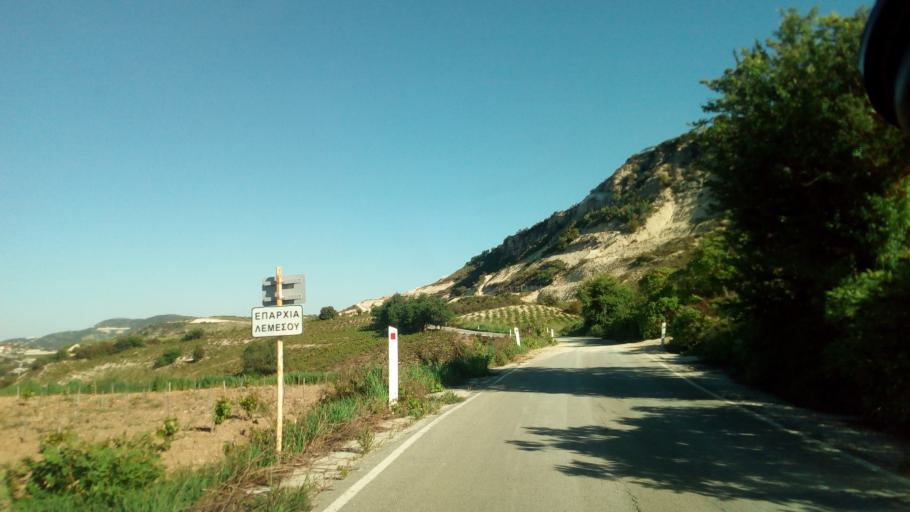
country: CY
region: Limassol
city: Pachna
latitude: 34.8658
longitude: 32.7816
